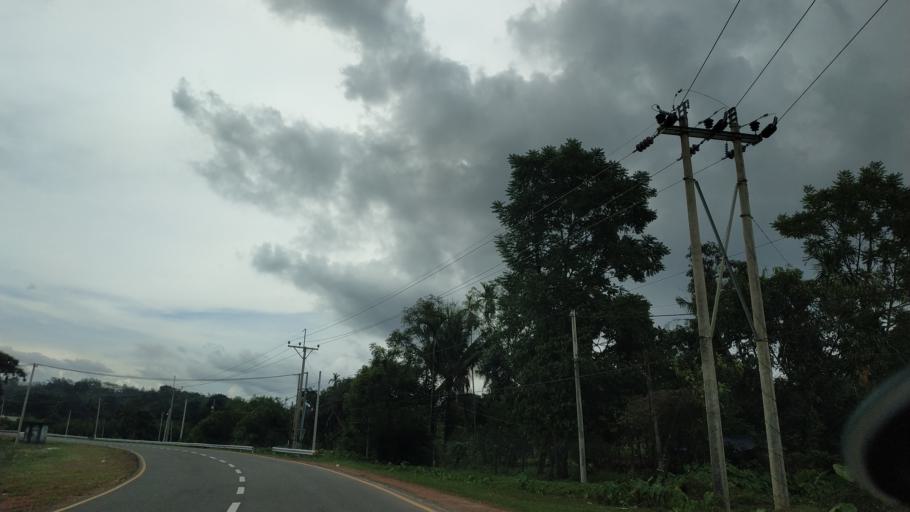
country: MM
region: Tanintharyi
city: Dawei
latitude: 14.0542
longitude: 98.2236
